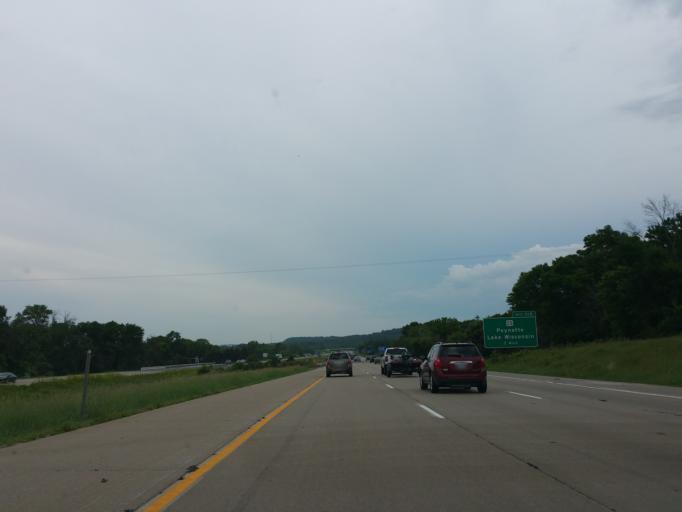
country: US
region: Wisconsin
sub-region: Columbia County
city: Poynette
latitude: 43.4072
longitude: -89.4673
